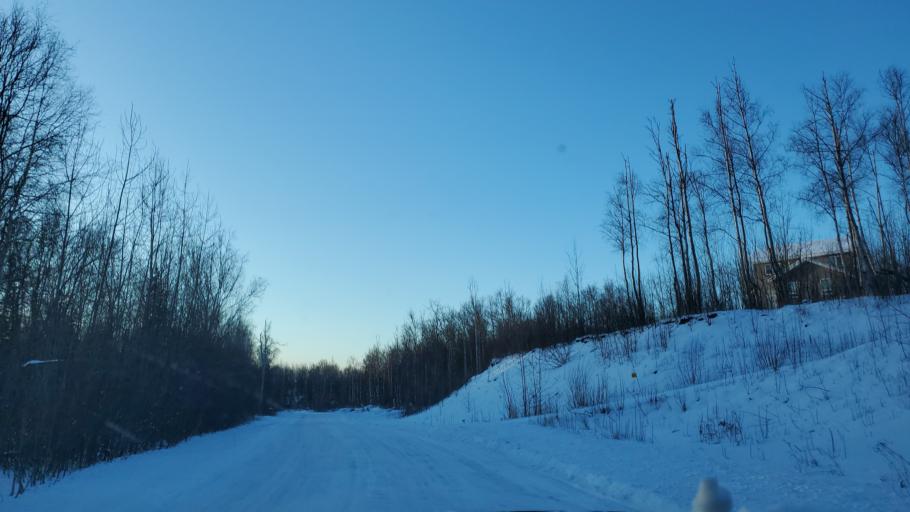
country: US
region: Alaska
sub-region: Matanuska-Susitna Borough
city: Lakes
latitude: 61.6376
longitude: -149.2931
